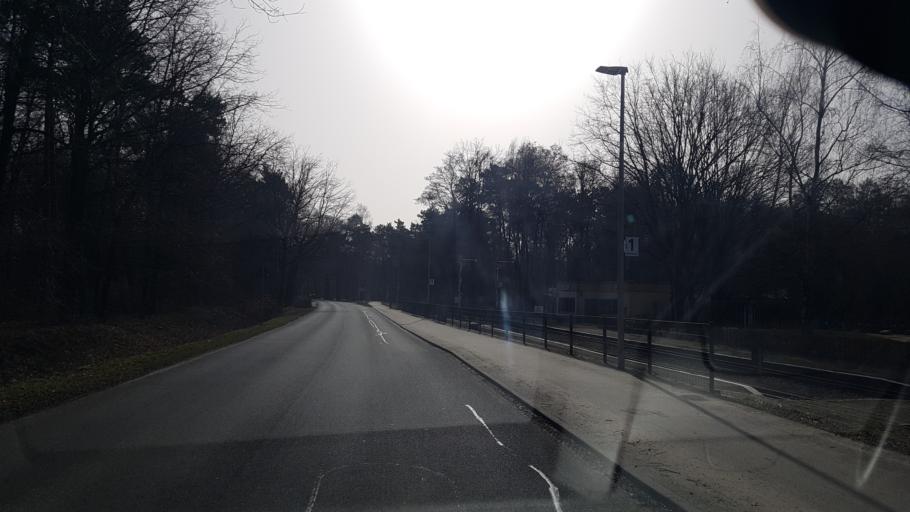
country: DE
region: Brandenburg
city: Cottbus
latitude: 51.7457
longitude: 14.3534
